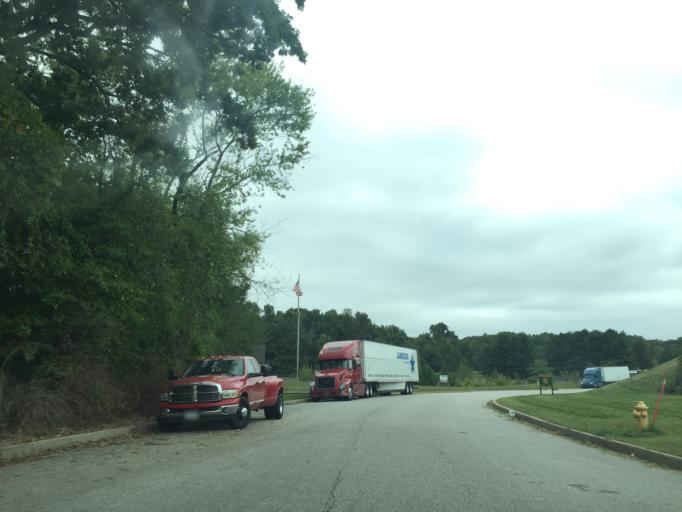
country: US
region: Maryland
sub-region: Harford County
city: Bel Air North
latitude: 39.5676
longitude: -76.3635
